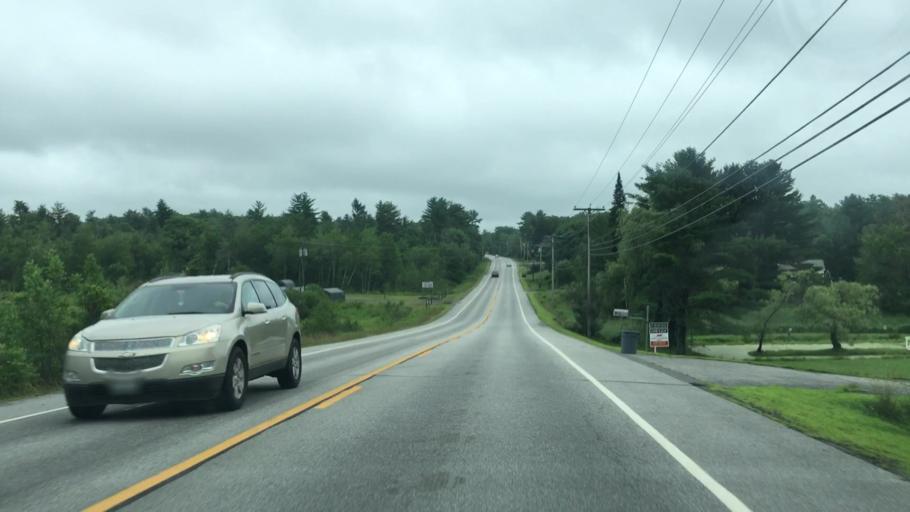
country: US
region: Maine
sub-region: Kennebec County
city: Chelsea
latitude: 44.2838
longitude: -69.6952
